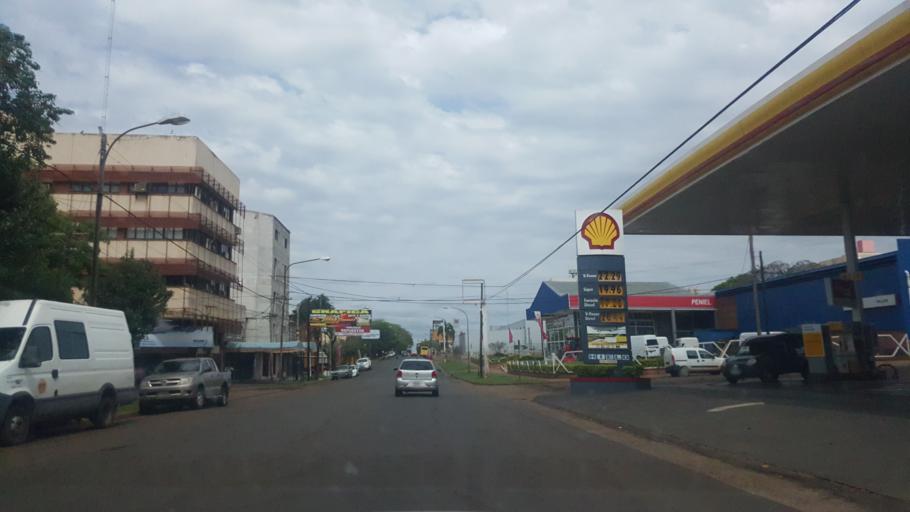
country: AR
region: Misiones
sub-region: Departamento de Capital
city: Posadas
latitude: -27.3912
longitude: -55.9085
